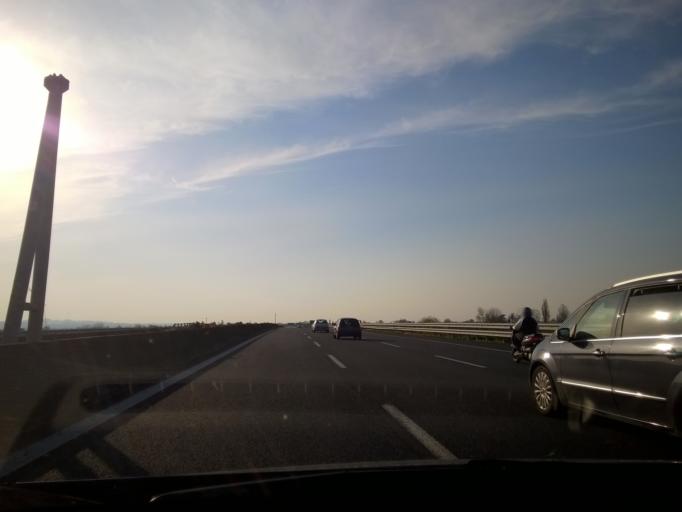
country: IT
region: Emilia-Romagna
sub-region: Provincia di Ravenna
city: Solarolo
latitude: 44.3504
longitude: 11.8270
